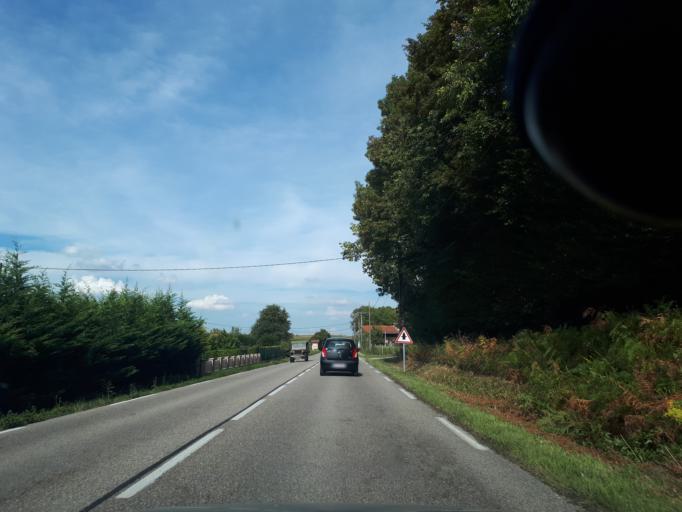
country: FR
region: Rhone-Alpes
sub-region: Departement de l'Isere
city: Chatonnay
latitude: 45.5309
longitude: 5.2207
